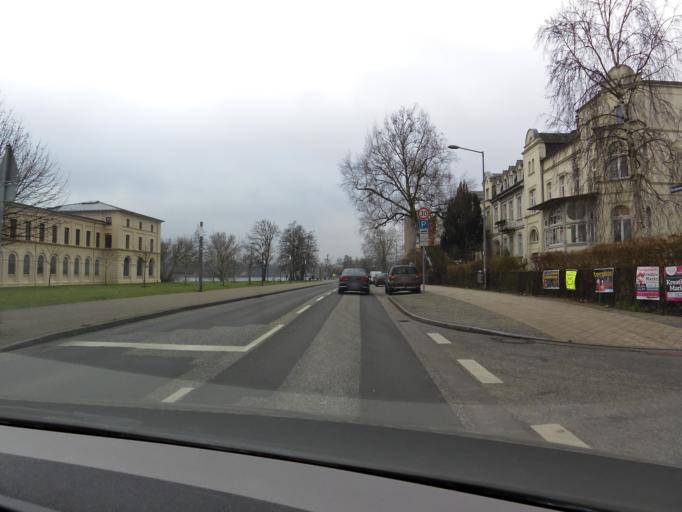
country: DE
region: Mecklenburg-Vorpommern
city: Altstadt
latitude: 53.6278
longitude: 11.4207
